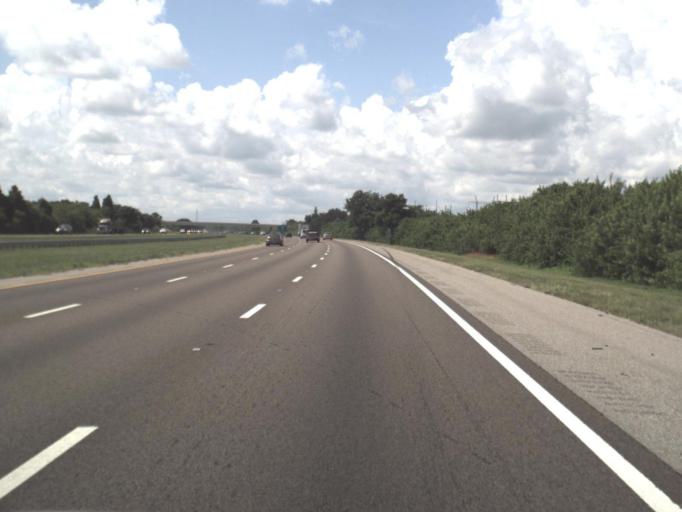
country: US
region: Florida
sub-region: Hillsborough County
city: Sun City Center
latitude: 27.7409
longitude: -82.3829
